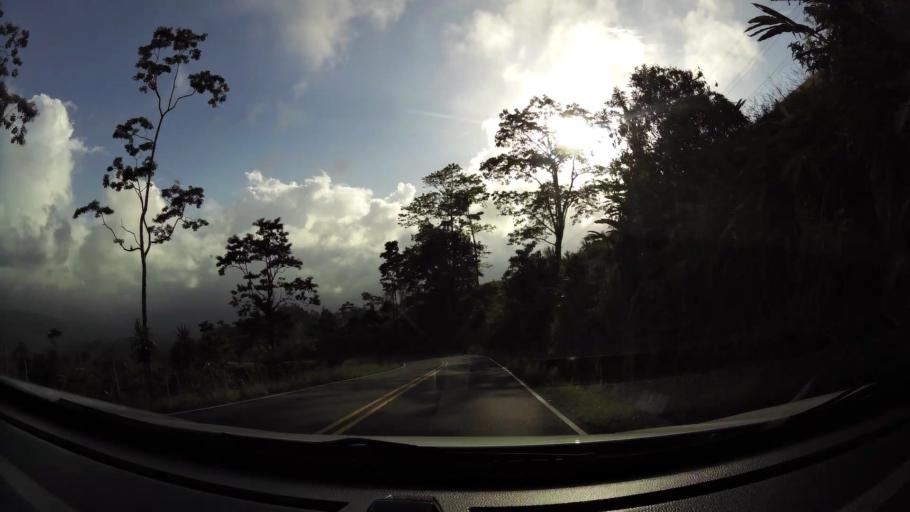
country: CR
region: Limon
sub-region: Canton de Siquirres
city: Siquirres
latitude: 10.0371
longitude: -83.5477
